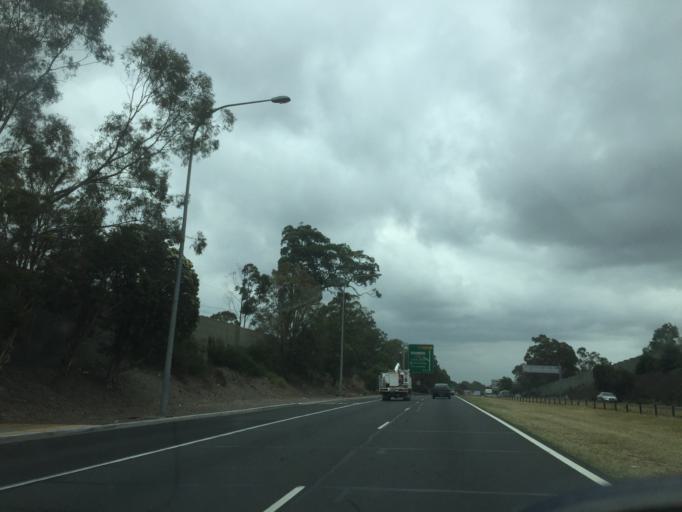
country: AU
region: New South Wales
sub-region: Parramatta
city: Northmead
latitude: -33.7714
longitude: 150.9845
